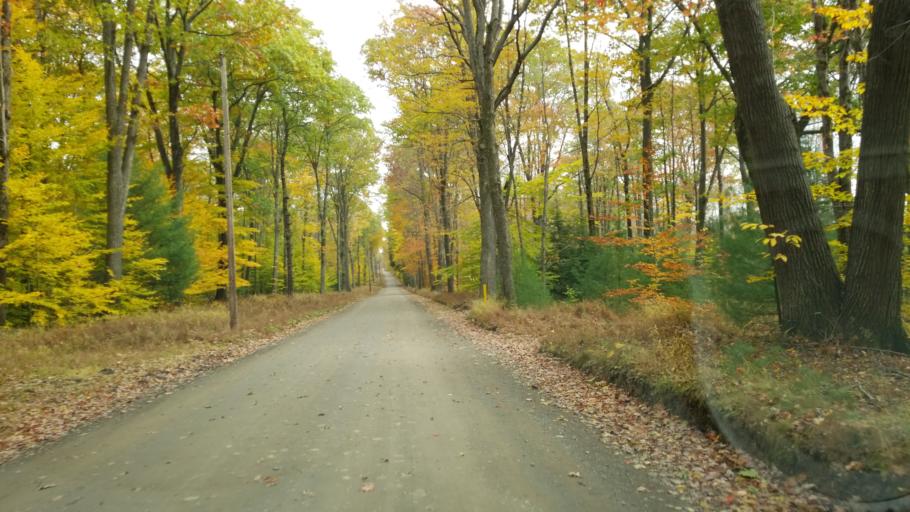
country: US
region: Pennsylvania
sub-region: Clearfield County
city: Shiloh
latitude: 41.1901
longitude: -78.3747
